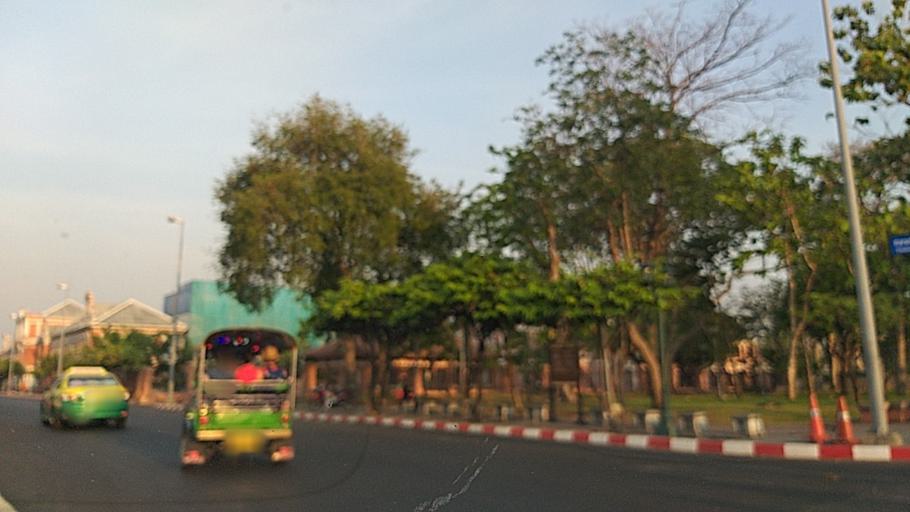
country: TH
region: Bangkok
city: Bangkok
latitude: 13.7511
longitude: 100.4939
